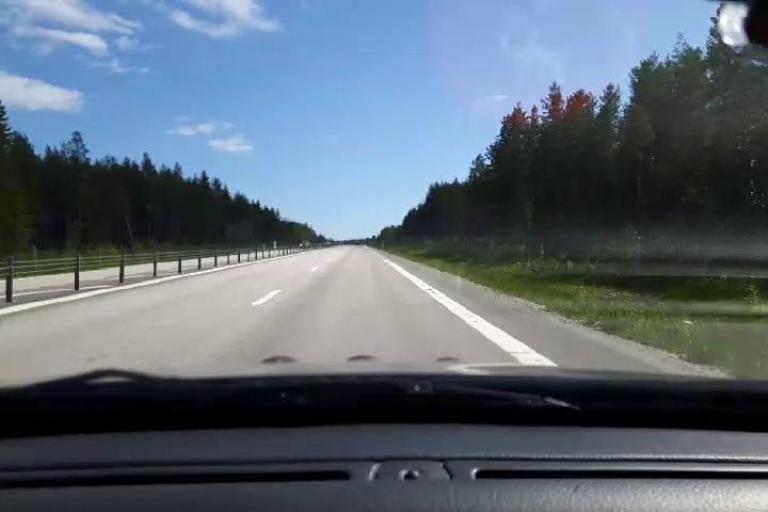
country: SE
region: Gaevleborg
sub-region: Hudiksvalls Kommun
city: Hudiksvall
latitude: 61.7067
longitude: 17.0505
